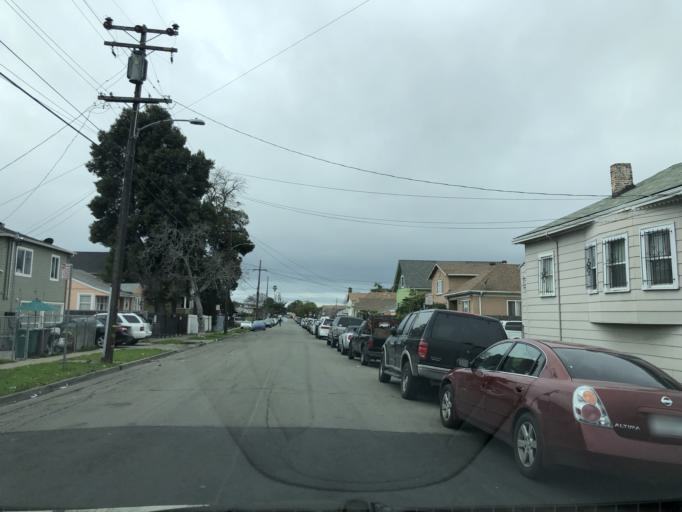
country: US
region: California
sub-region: Alameda County
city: San Leandro
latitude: 37.7497
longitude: -122.1769
